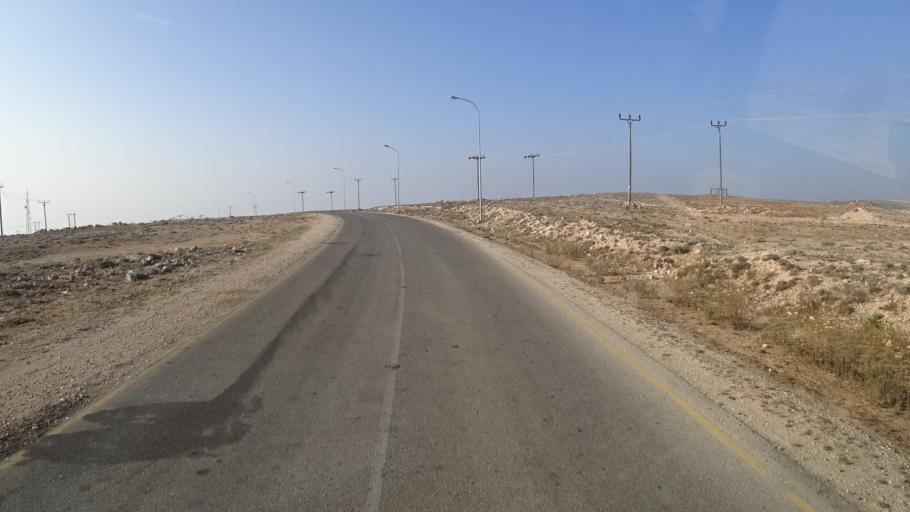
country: YE
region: Al Mahrah
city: Hawf
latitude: 16.7719
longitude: 53.2285
